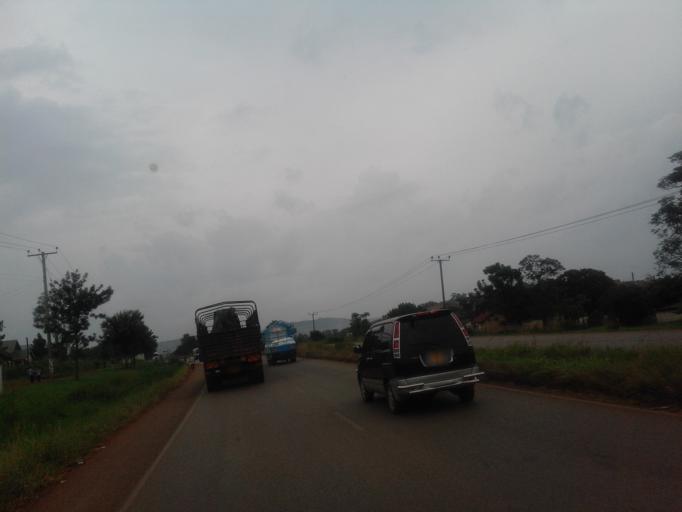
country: UG
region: Eastern Region
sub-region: Jinja District
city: Jinja
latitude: 0.4453
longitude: 33.2178
